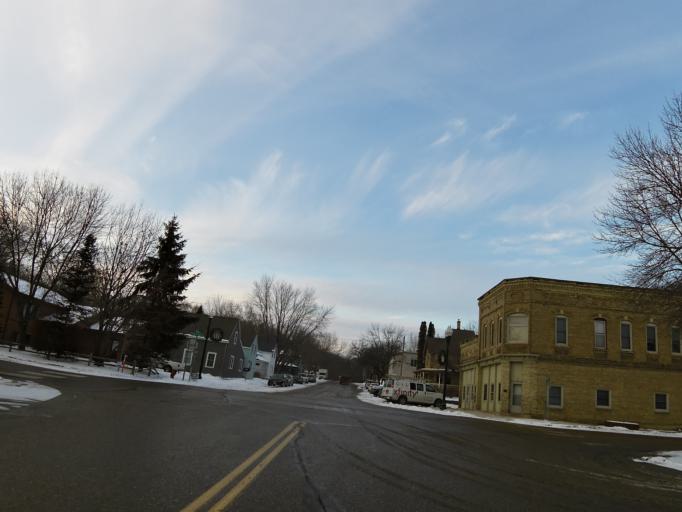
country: US
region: Minnesota
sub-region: Carver County
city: Carver
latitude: 44.7635
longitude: -93.6255
